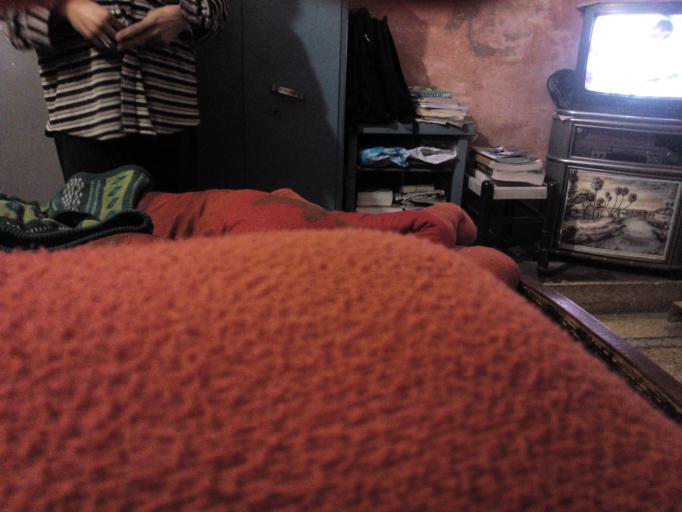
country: IN
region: Punjab
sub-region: Amritsar
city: Amritsar
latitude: 31.6349
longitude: 74.8472
